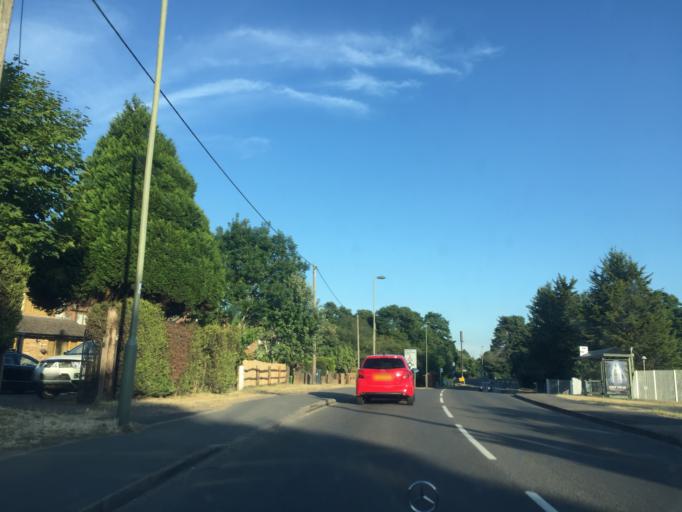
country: GB
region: England
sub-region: Surrey
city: Frimley
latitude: 51.3116
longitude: -0.7357
